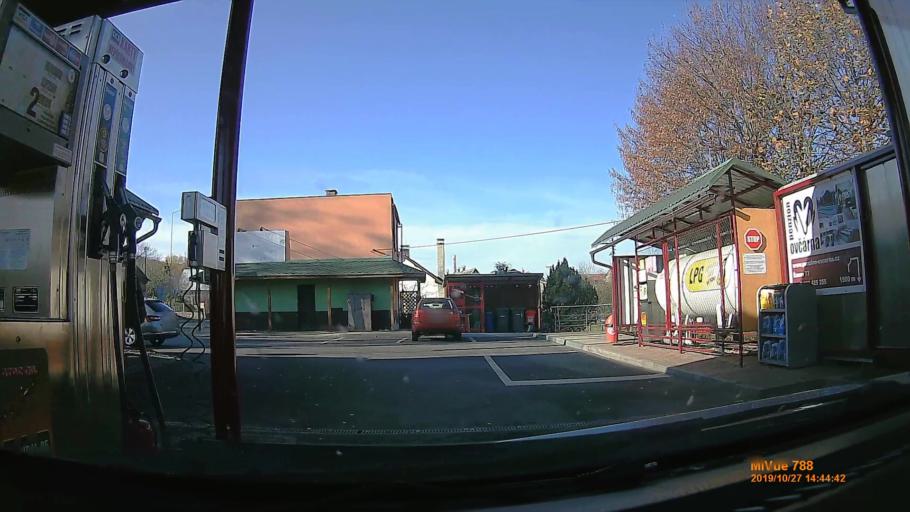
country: CZ
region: Pardubicky
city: Cervena Voda
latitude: 50.0430
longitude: 16.7416
